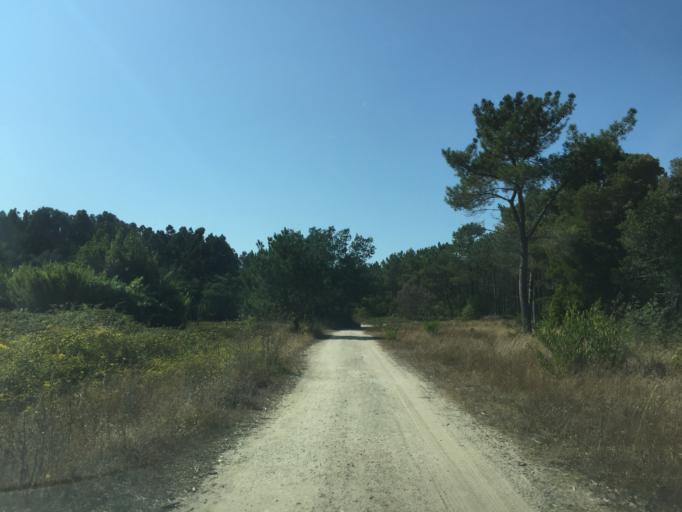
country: PT
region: Coimbra
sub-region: Figueira da Foz
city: Tavarede
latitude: 40.2276
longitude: -8.8517
